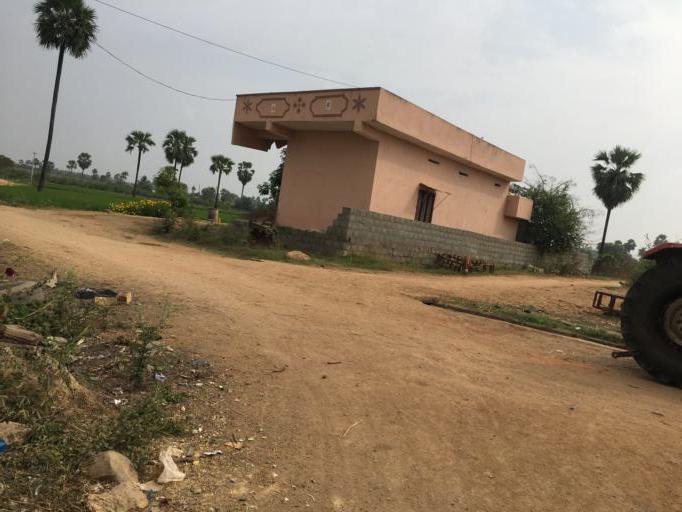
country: IN
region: Telangana
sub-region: Nalgonda
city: Nalgonda
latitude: 17.1590
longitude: 79.3903
